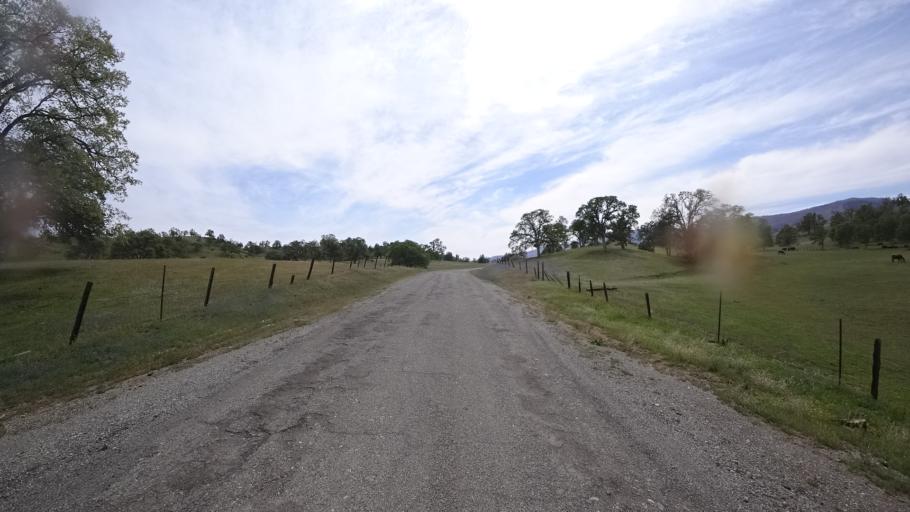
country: US
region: California
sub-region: Glenn County
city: Willows
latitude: 39.6258
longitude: -122.5901
